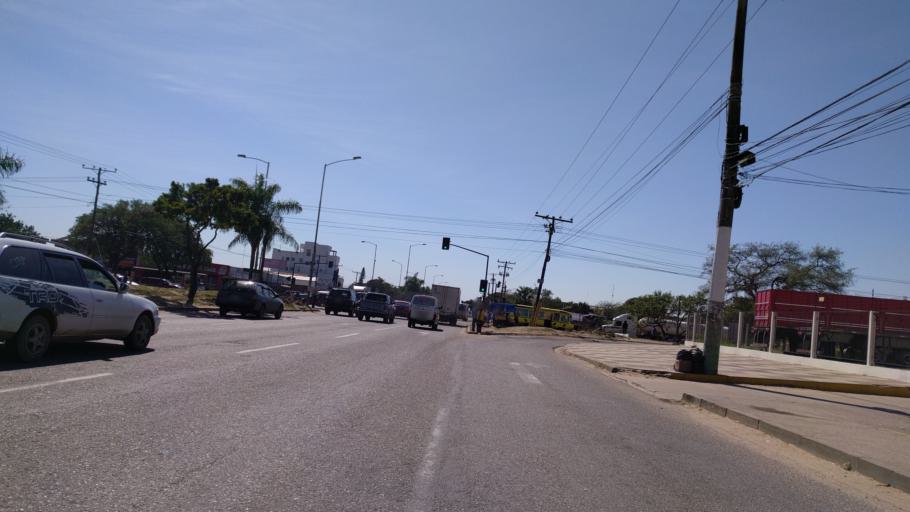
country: BO
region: Santa Cruz
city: Santa Cruz de la Sierra
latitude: -17.8169
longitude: -63.2138
